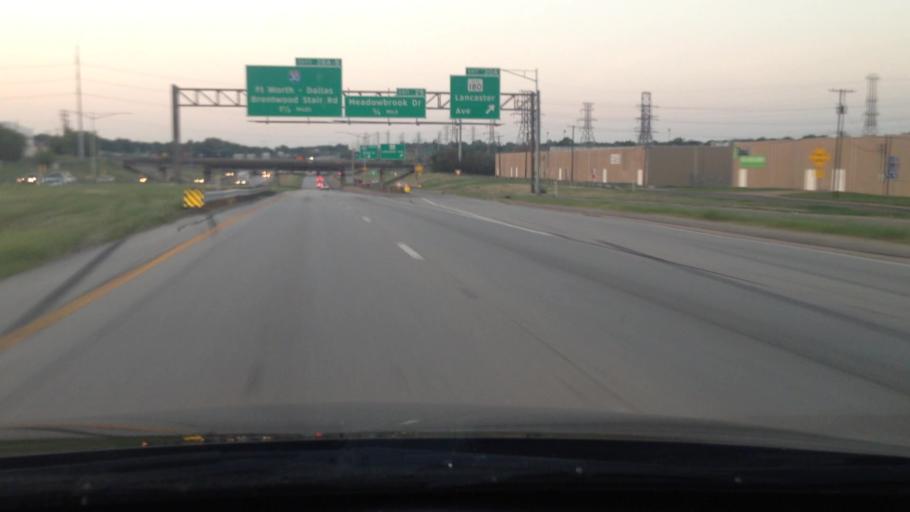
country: US
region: Texas
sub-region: Tarrant County
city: Pantego
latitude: 32.7303
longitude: -97.2251
